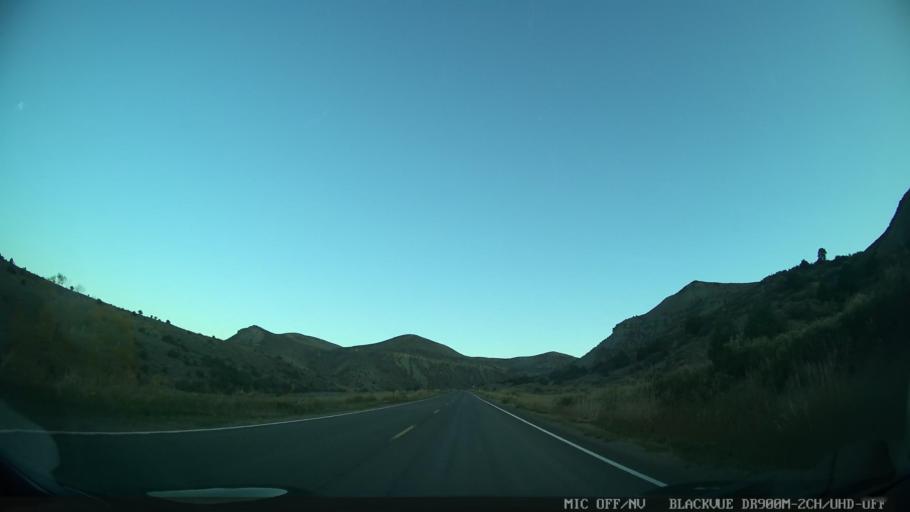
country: US
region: Colorado
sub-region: Eagle County
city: Edwards
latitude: 39.7677
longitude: -106.6798
